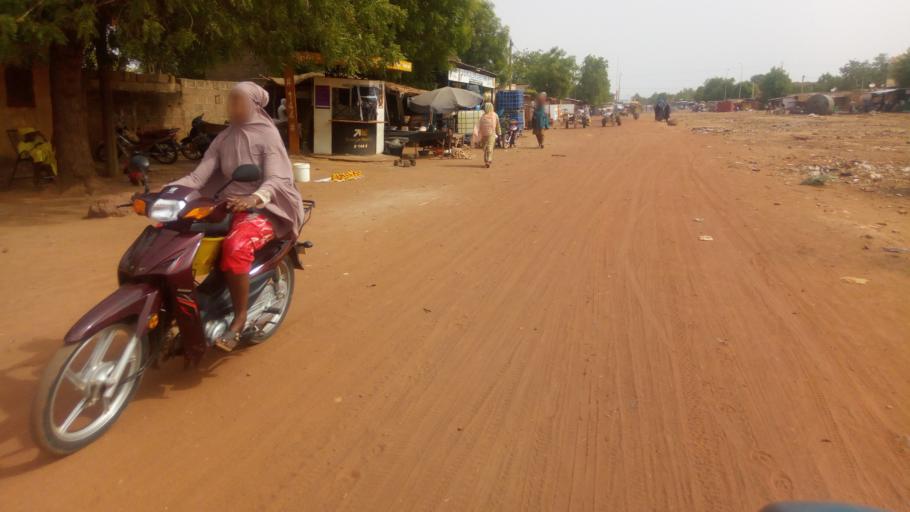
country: ML
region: Segou
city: Segou
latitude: 13.4291
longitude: -6.2608
